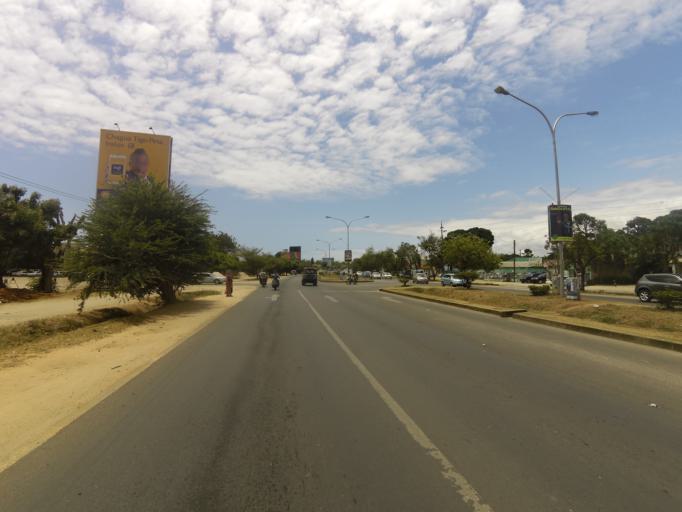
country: TZ
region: Dar es Salaam
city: Magomeni
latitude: -6.7776
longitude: 39.2682
